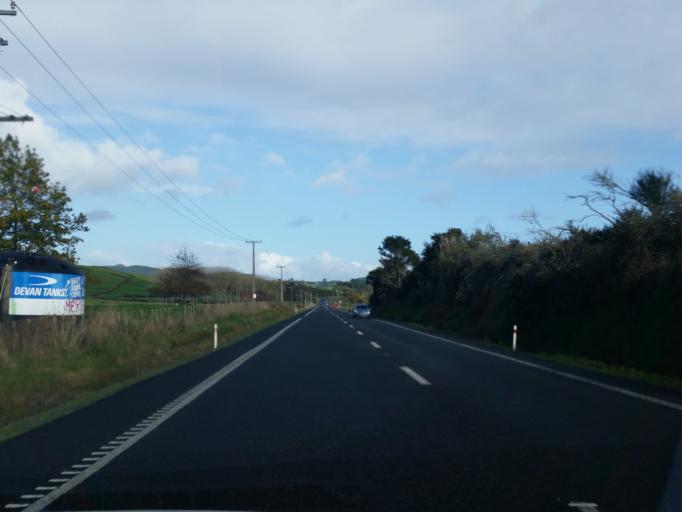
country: NZ
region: Waikato
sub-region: Hauraki District
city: Ngatea
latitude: -37.2846
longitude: 175.3959
